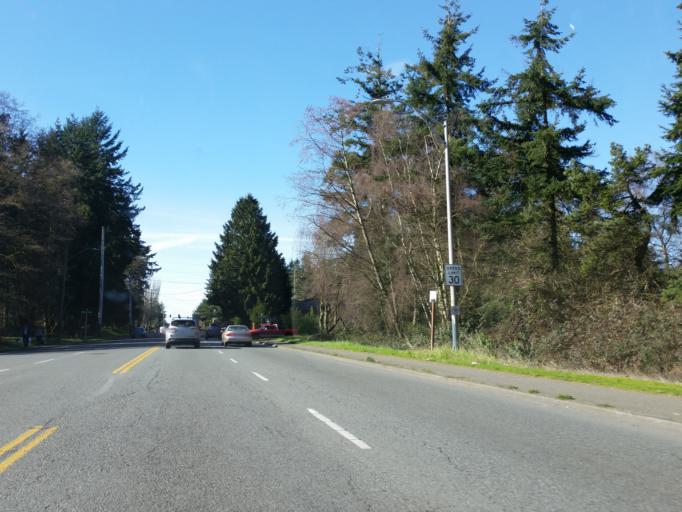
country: US
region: Washington
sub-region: King County
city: Shoreline
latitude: 47.7232
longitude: -122.3251
